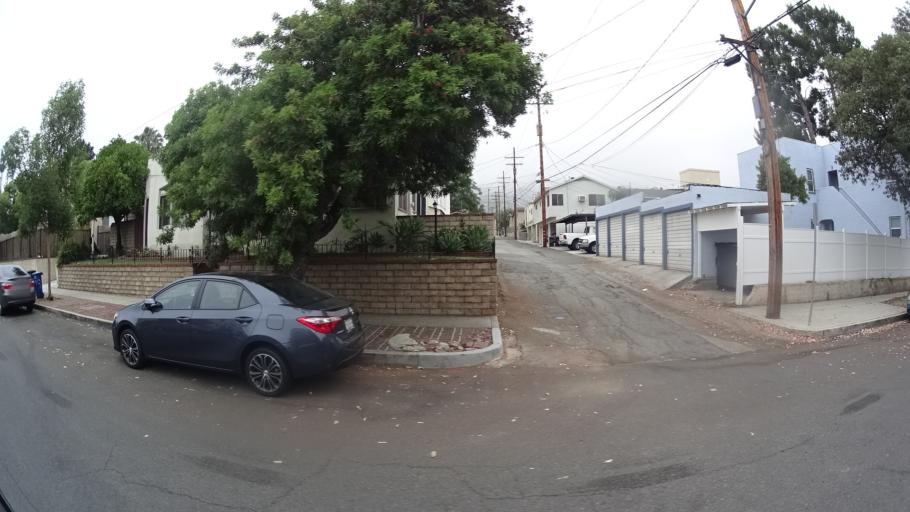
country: US
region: California
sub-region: Los Angeles County
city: Burbank
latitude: 34.1835
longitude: -118.2983
